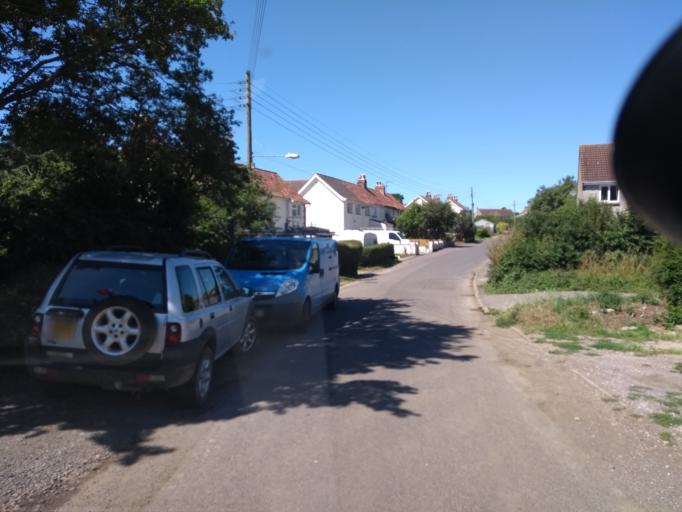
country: GB
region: England
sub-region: Somerset
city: Curry Rivel
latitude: 51.0274
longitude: -2.8655
